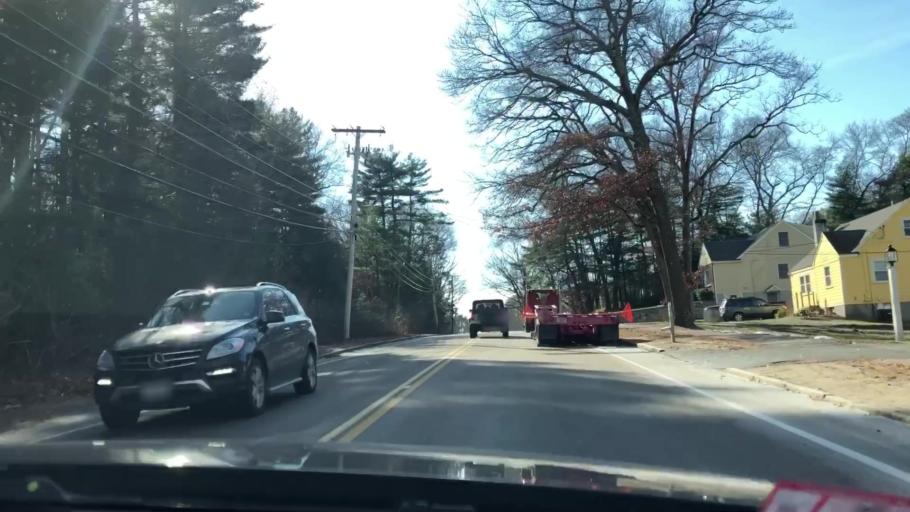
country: US
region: Massachusetts
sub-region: Norfolk County
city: Walpole
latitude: 42.1345
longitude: -71.2396
